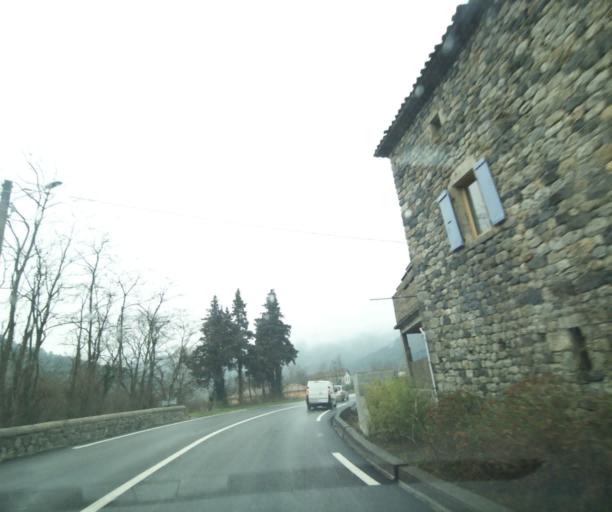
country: FR
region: Rhone-Alpes
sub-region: Departement de l'Ardeche
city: Jaujac
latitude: 44.6632
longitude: 4.2962
